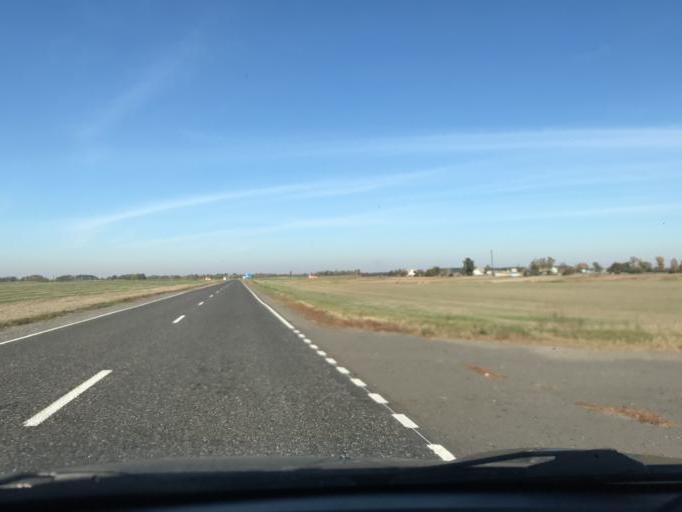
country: BY
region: Gomel
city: Brahin
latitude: 51.6638
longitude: 30.4266
